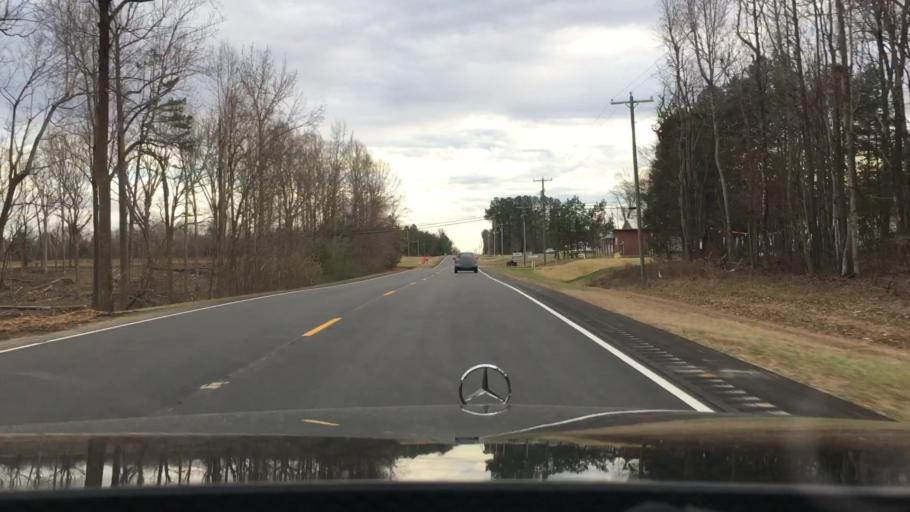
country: US
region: North Carolina
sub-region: Alamance County
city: Mebane
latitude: 36.2566
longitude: -79.1931
